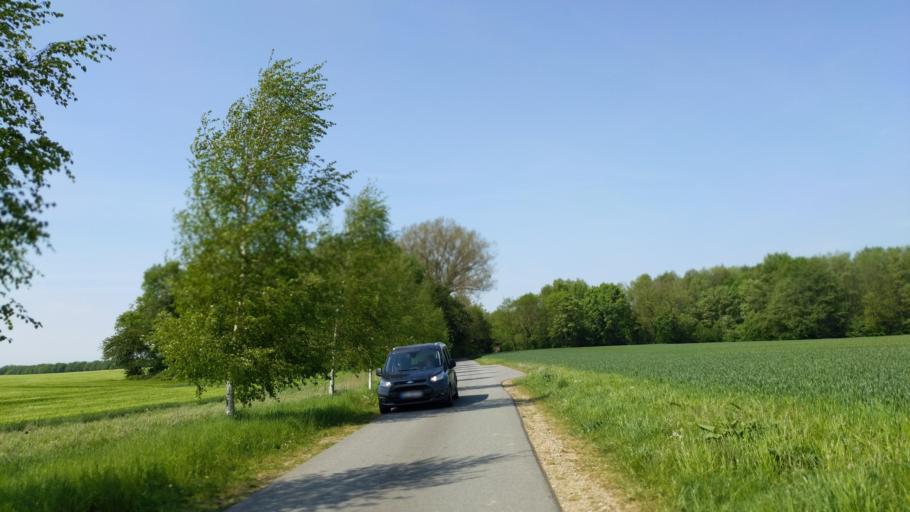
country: DE
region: Mecklenburg-Vorpommern
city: Selmsdorf
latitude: 53.8788
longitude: 10.8951
